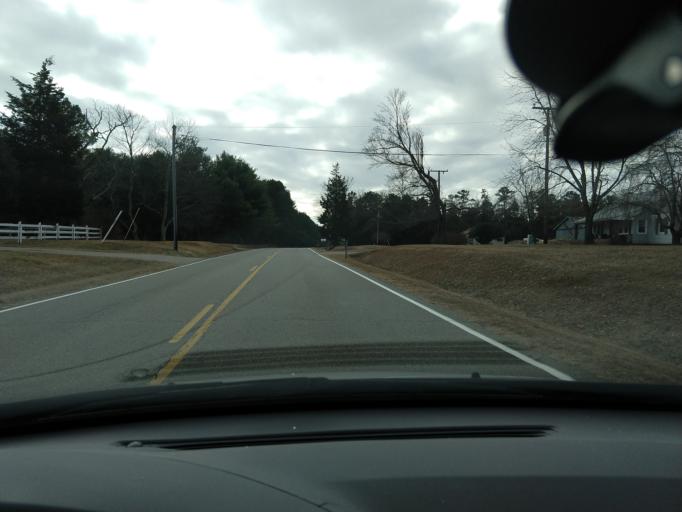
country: US
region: Virginia
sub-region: Henrico County
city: Fort Lee
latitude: 37.4343
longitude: -77.3662
